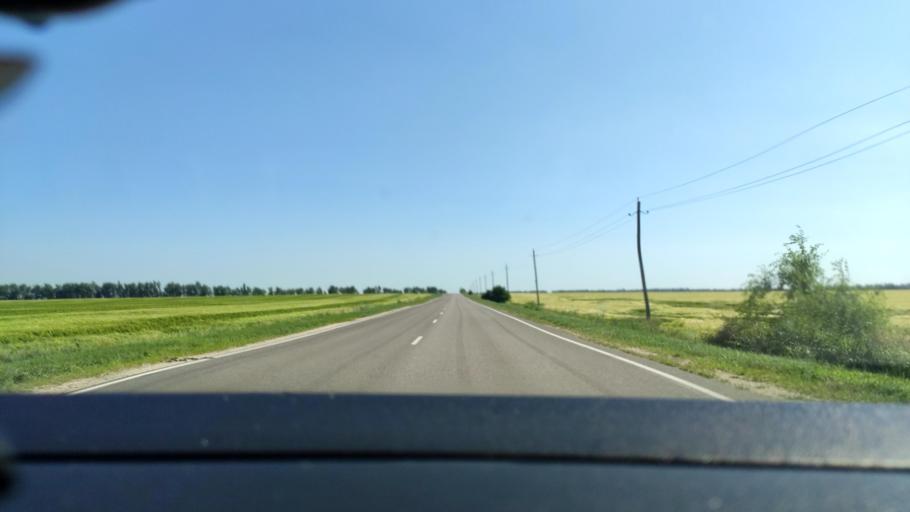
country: RU
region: Voronezj
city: Novaya Usman'
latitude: 51.5636
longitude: 39.3754
